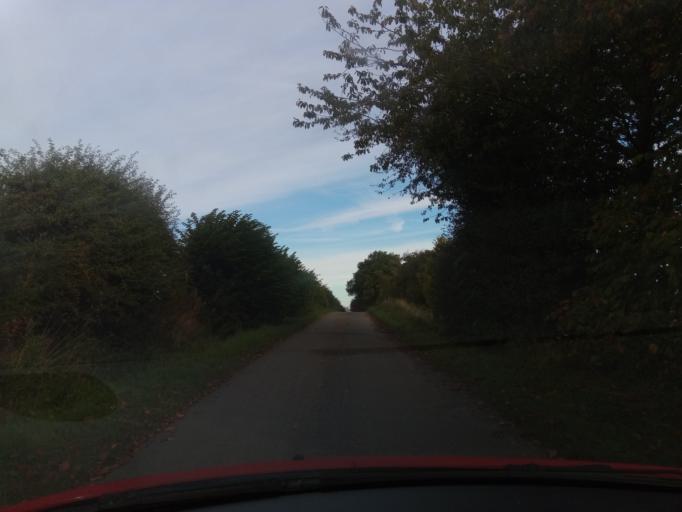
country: GB
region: Scotland
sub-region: The Scottish Borders
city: Jedburgh
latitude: 55.4815
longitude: -2.4990
